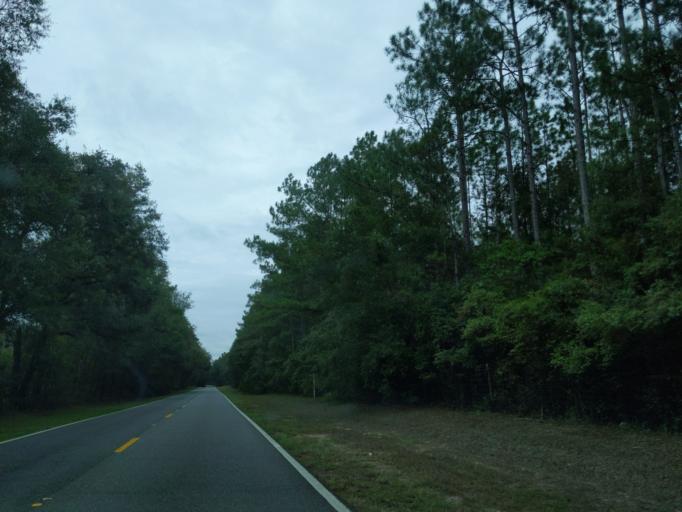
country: US
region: Florida
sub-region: Leon County
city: Woodville
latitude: 30.3674
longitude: -84.1574
